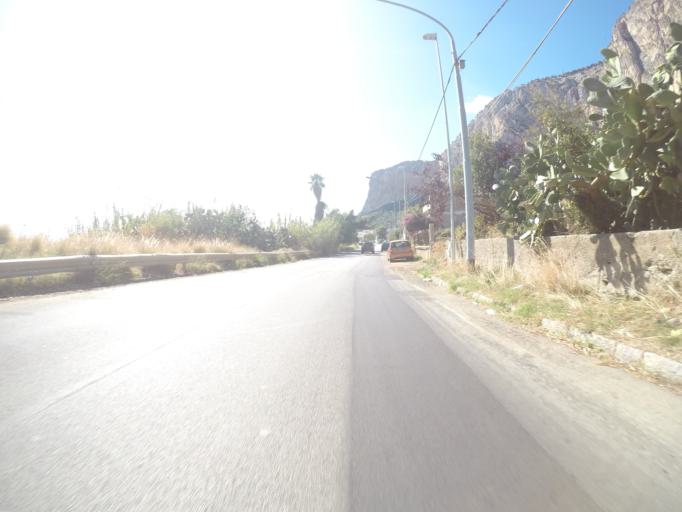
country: IT
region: Sicily
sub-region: Palermo
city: Palermo
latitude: 38.1705
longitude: 13.3667
